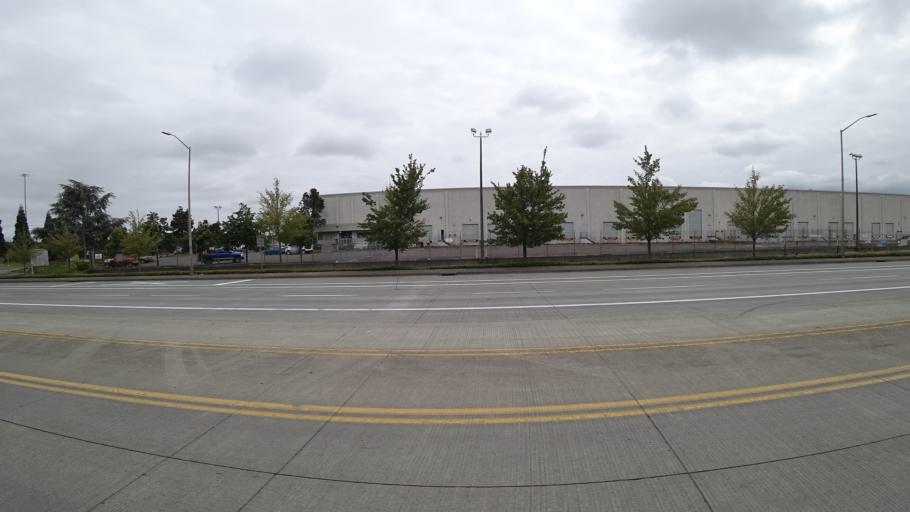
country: US
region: Washington
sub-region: Clark County
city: Lake Shore
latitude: 45.6356
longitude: -122.7551
